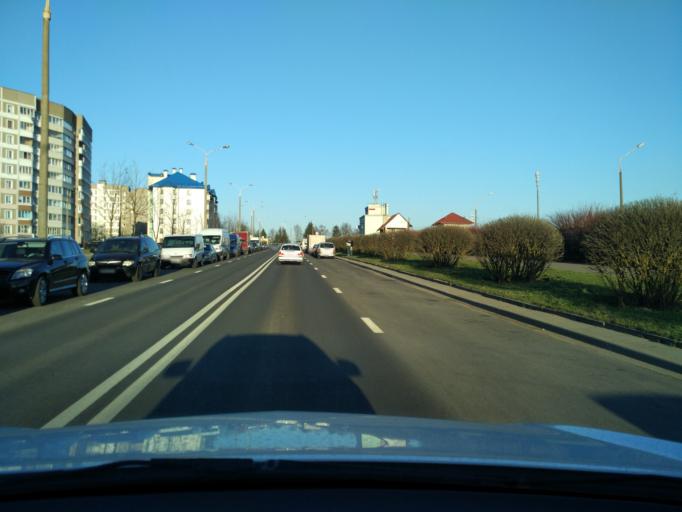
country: BY
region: Minsk
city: Shchomyslitsa
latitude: 53.8447
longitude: 27.4603
